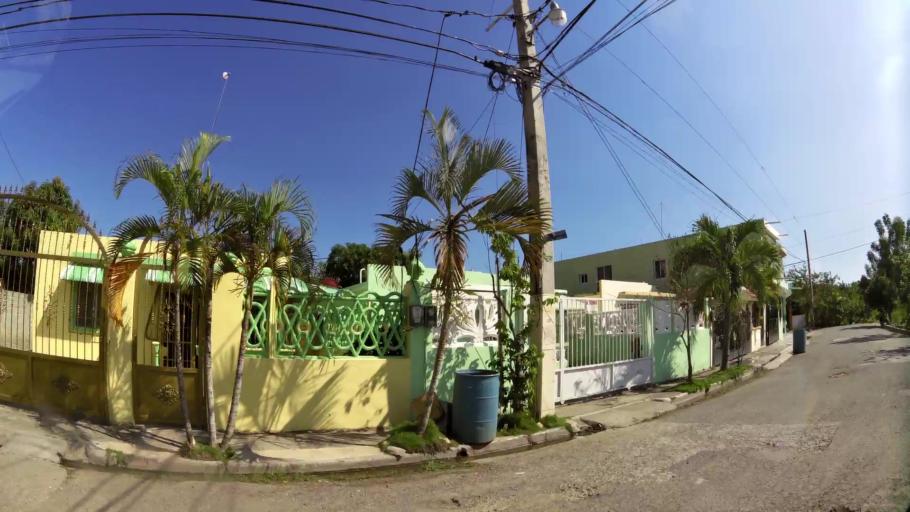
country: DO
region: Santo Domingo
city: Santo Domingo Oeste
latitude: 18.4723
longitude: -70.0091
